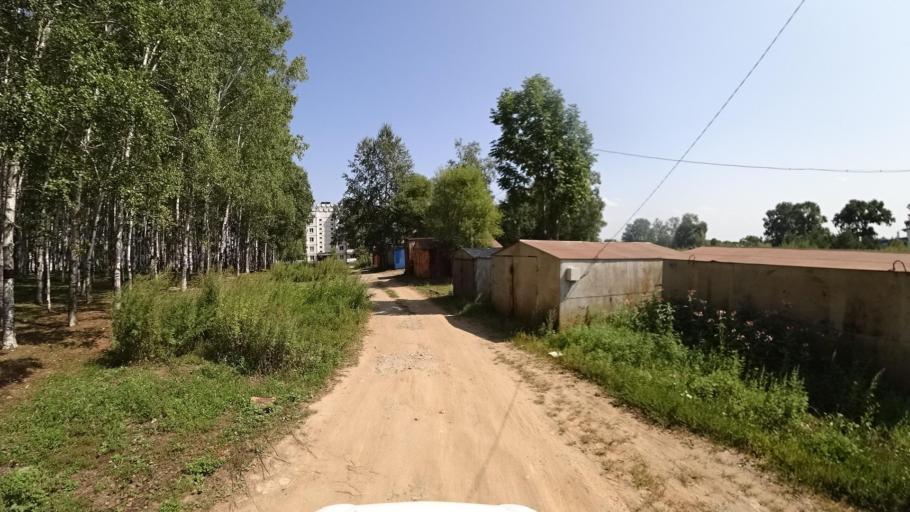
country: RU
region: Khabarovsk Krai
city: Khor
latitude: 47.9641
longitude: 135.1166
